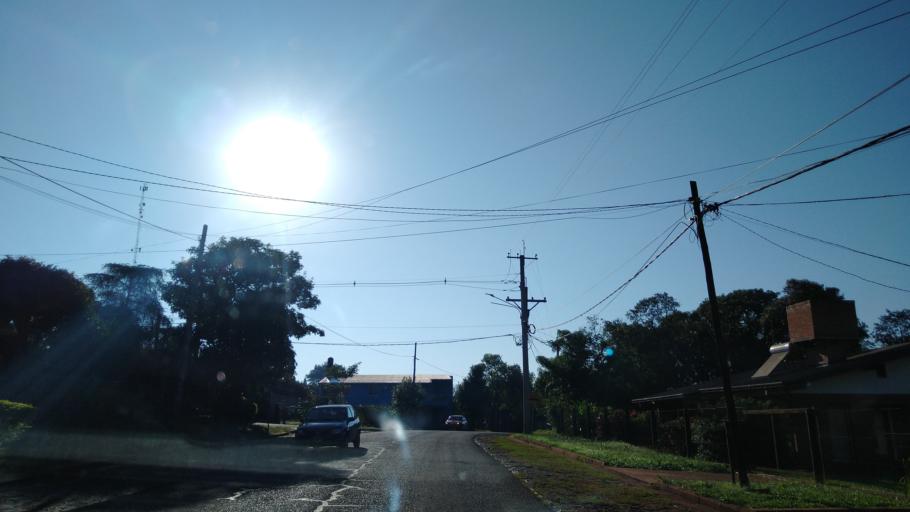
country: AR
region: Misiones
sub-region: Departamento de Montecarlo
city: Montecarlo
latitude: -26.5699
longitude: -54.7595
